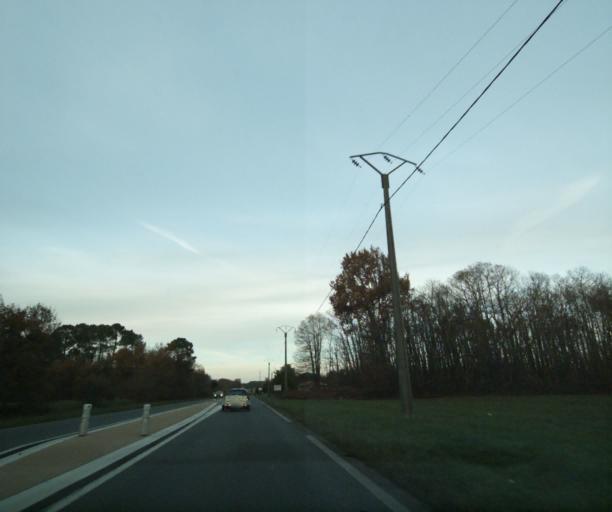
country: FR
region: Aquitaine
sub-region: Departement de la Gironde
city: Bazas
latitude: 44.4647
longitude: -0.2303
